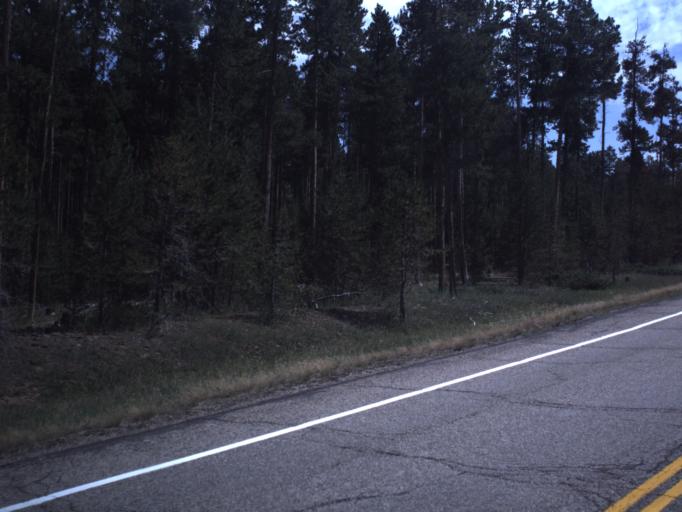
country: US
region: Utah
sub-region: Daggett County
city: Manila
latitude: 40.8409
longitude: -109.6511
